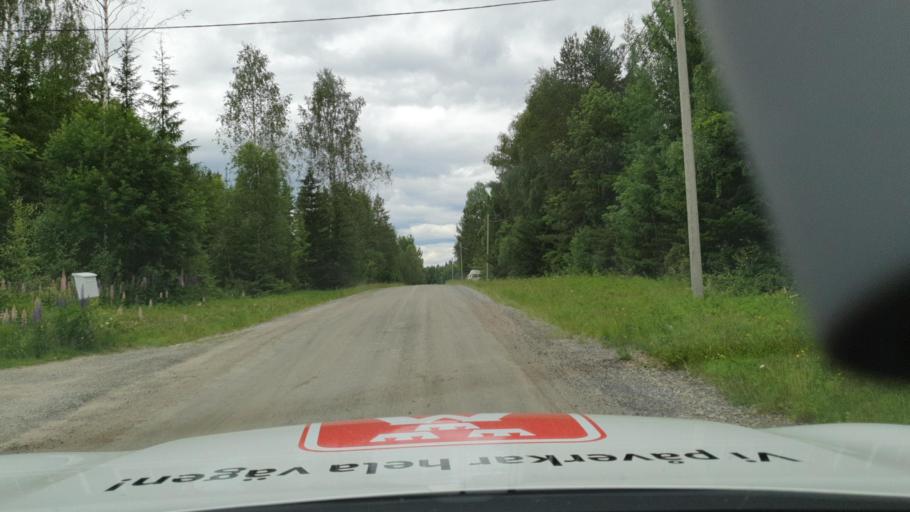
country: SE
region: Vaesterbotten
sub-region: Bjurholms Kommun
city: Bjurholm
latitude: 63.7358
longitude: 19.2924
